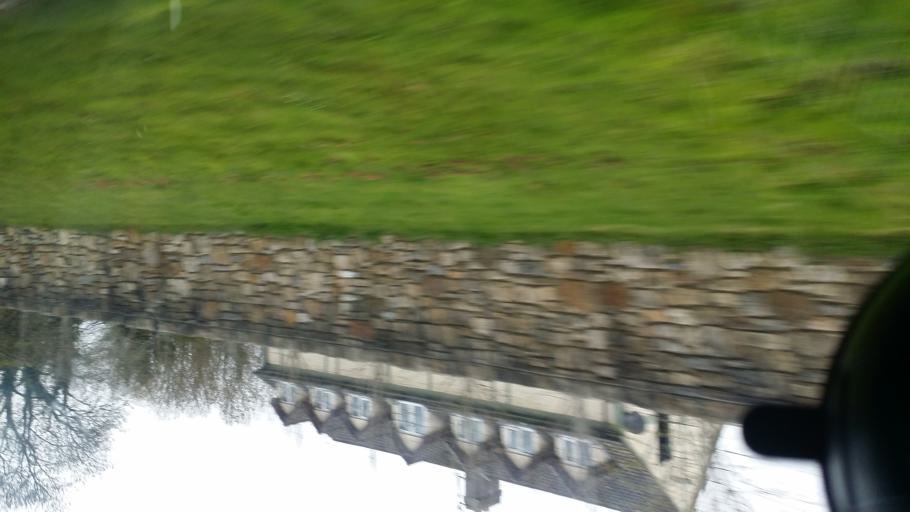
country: IE
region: Ulster
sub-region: An Cabhan
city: Belturbet
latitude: 54.0944
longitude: -7.4690
